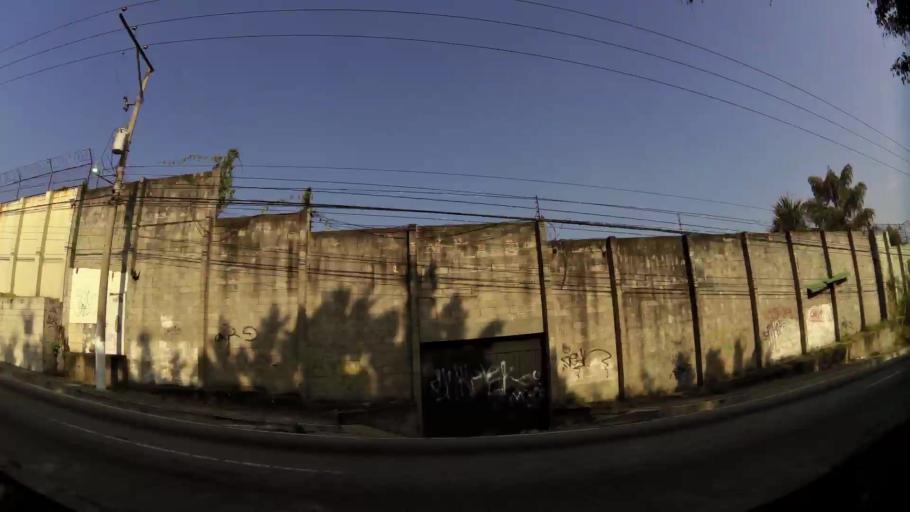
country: SV
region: San Salvador
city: San Salvador
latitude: 13.6781
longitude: -89.2173
